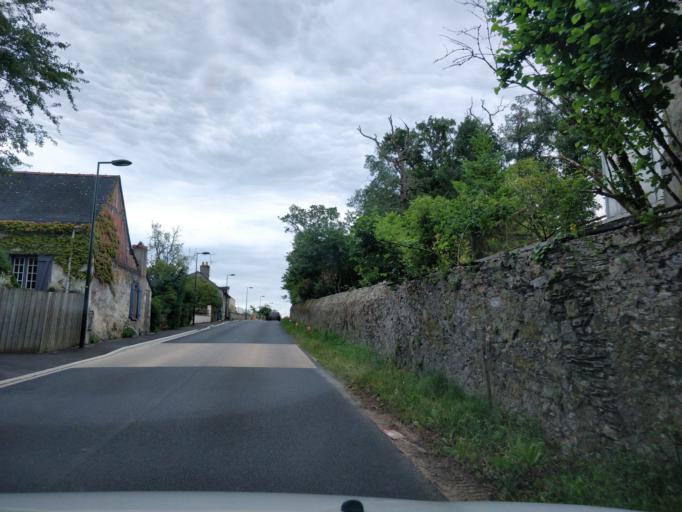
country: FR
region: Pays de la Loire
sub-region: Departement de Maine-et-Loire
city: Feneu
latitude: 47.5687
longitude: -0.5893
